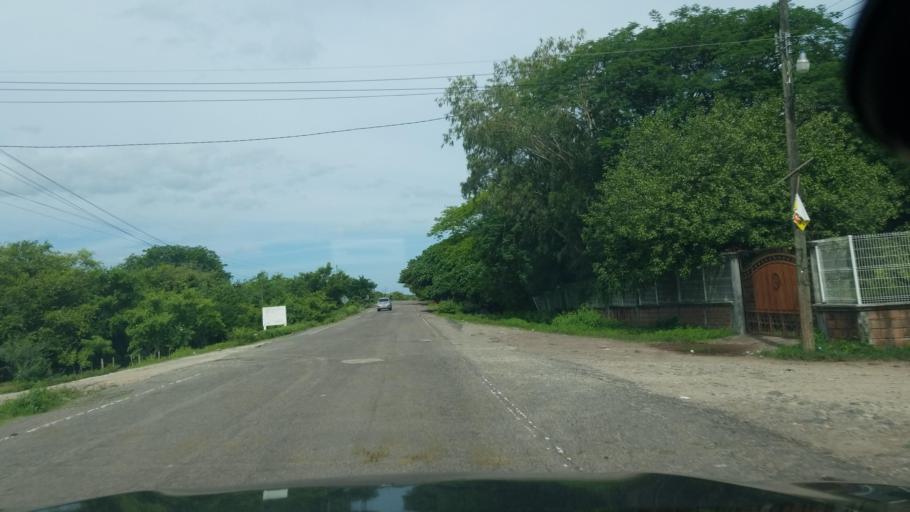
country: HN
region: Choluteca
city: Santa Ana de Yusguare
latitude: 13.3659
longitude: -87.0816
